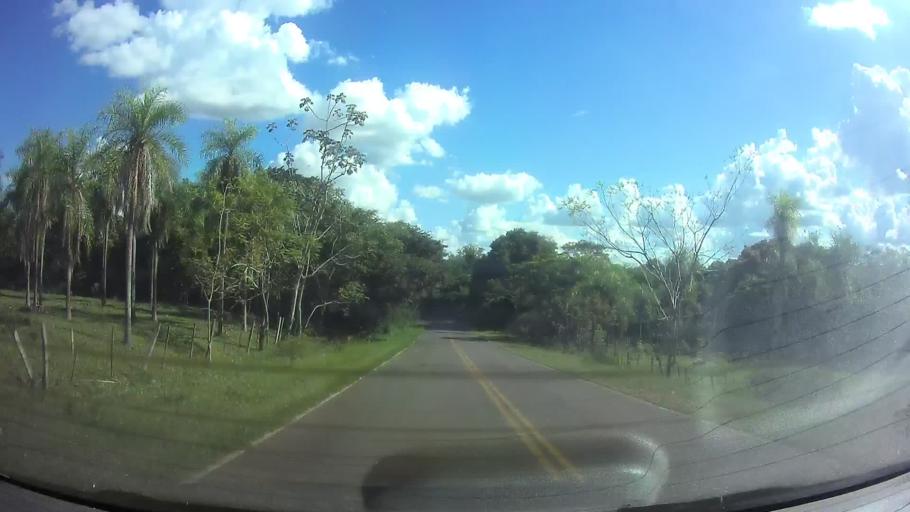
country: PY
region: Paraguari
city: Sapucai
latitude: -25.6644
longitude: -56.8574
